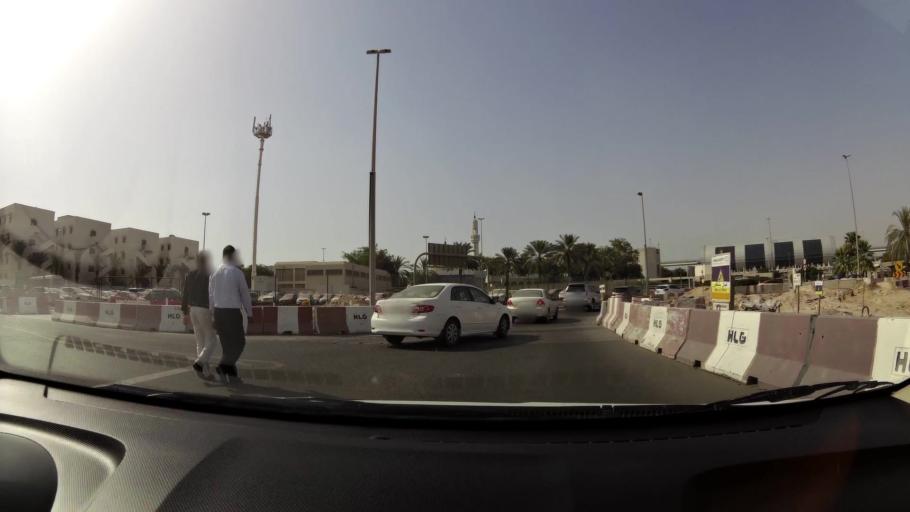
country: AE
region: Ash Shariqah
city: Sharjah
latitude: 25.2461
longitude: 55.3510
